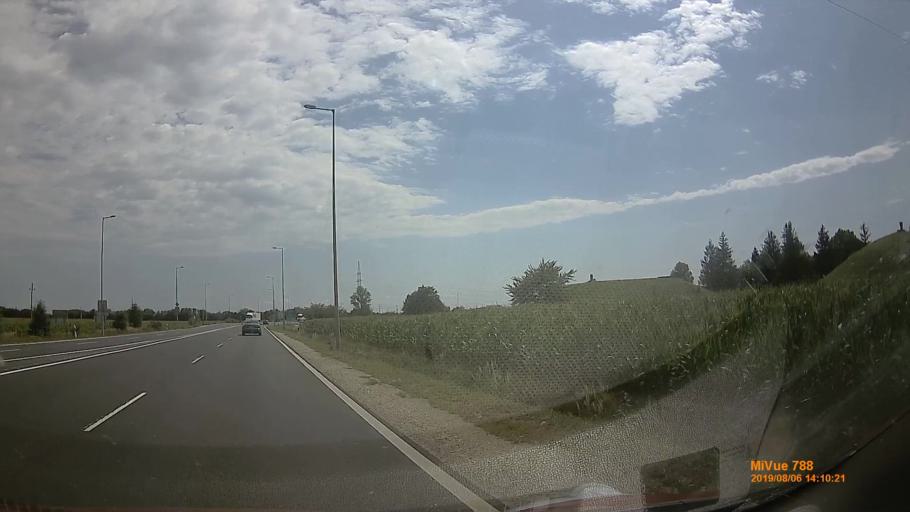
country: HU
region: Vas
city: Szombathely
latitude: 47.2253
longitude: 16.6572
